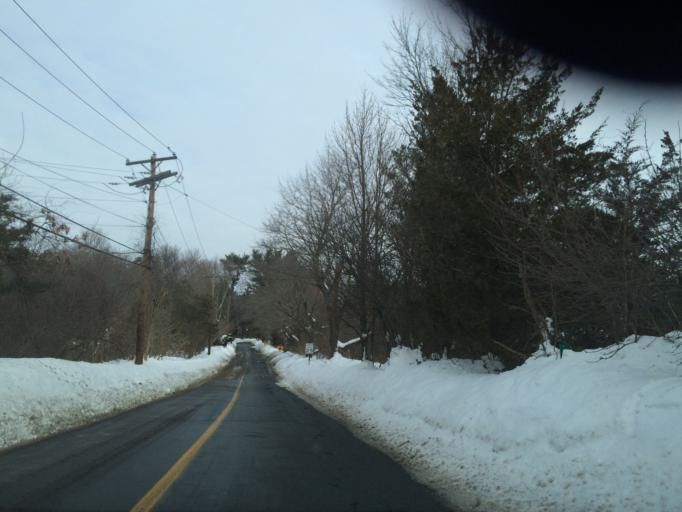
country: US
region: Massachusetts
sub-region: Middlesex County
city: Weston
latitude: 42.3354
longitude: -71.3143
